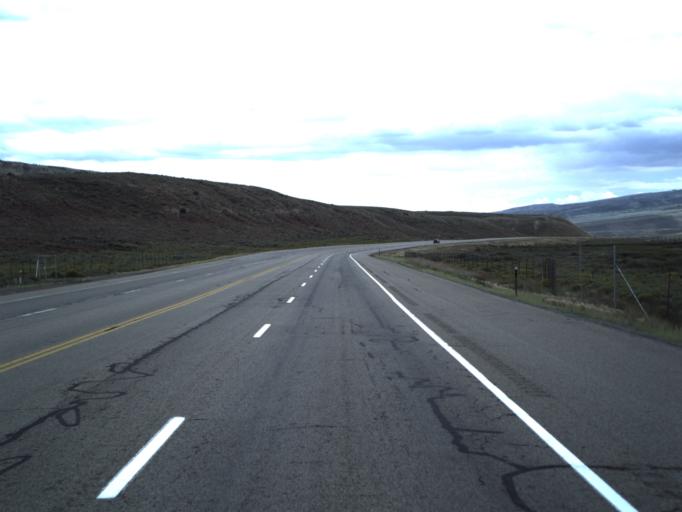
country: US
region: Utah
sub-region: Carbon County
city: Helper
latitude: 39.8764
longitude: -111.0376
